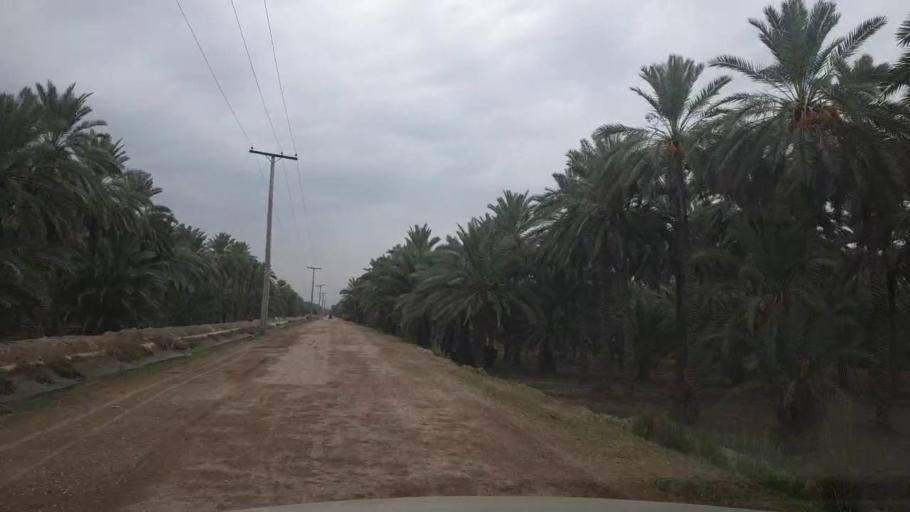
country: PK
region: Sindh
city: Sukkur
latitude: 27.6134
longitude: 68.8179
